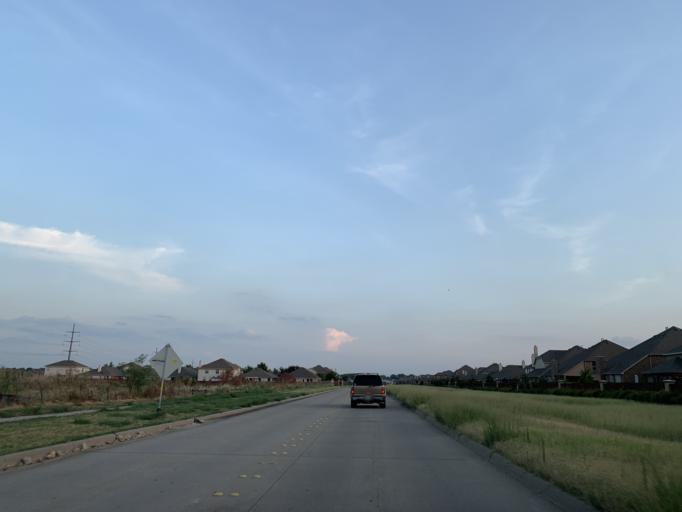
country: US
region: Texas
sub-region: Tarrant County
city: Keller
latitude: 32.9630
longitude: -97.2645
